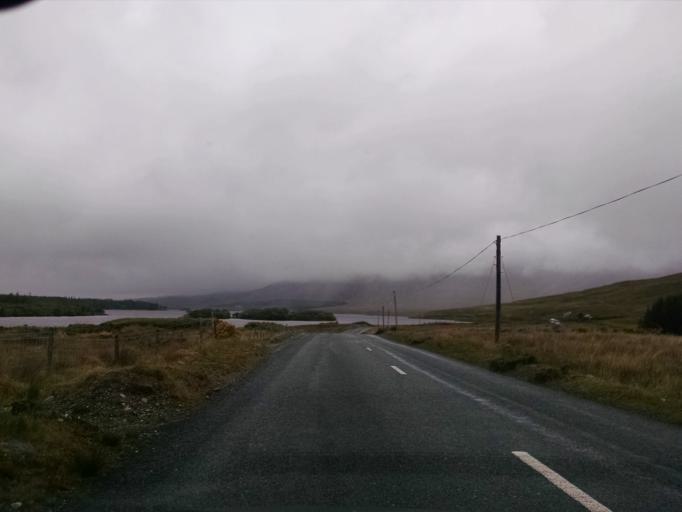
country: IE
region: Connaught
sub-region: County Galway
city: Clifden
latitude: 53.4908
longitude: -9.7387
